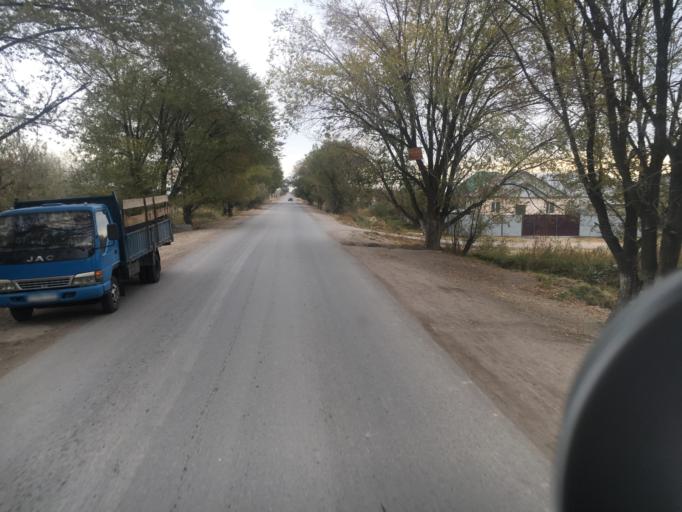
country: KZ
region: Almaty Oblysy
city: Energeticheskiy
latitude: 43.5860
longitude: 77.0621
